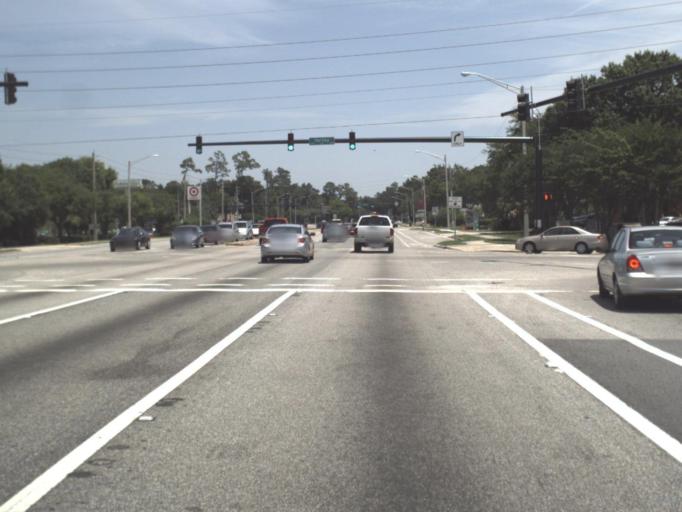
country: US
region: Florida
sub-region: Saint Johns County
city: Fruit Cove
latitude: 30.1852
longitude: -81.6282
